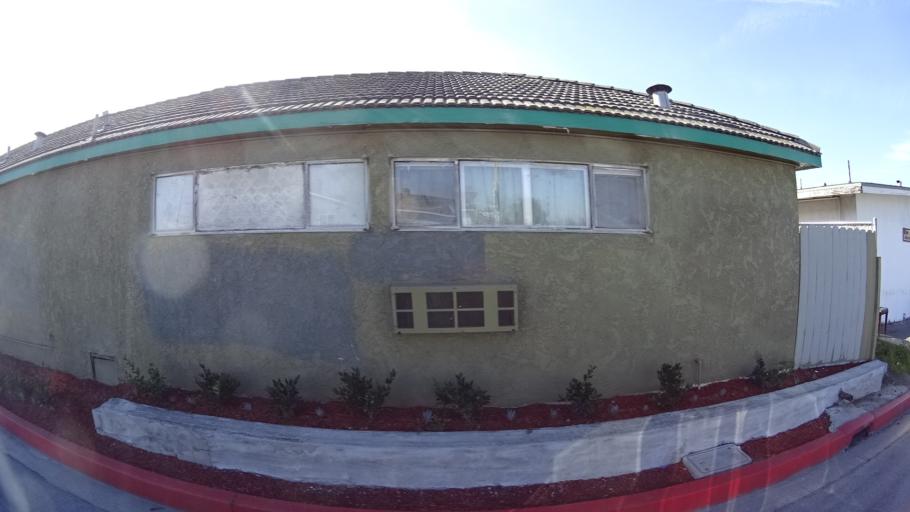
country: US
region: California
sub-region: Orange County
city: Anaheim
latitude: 33.8508
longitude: -117.9252
